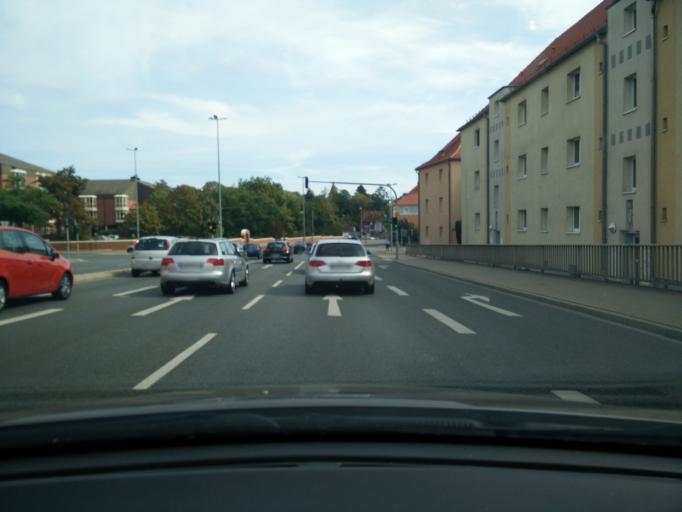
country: DE
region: Bavaria
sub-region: Regierungsbezirk Mittelfranken
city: Furth
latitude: 49.4821
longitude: 10.9686
